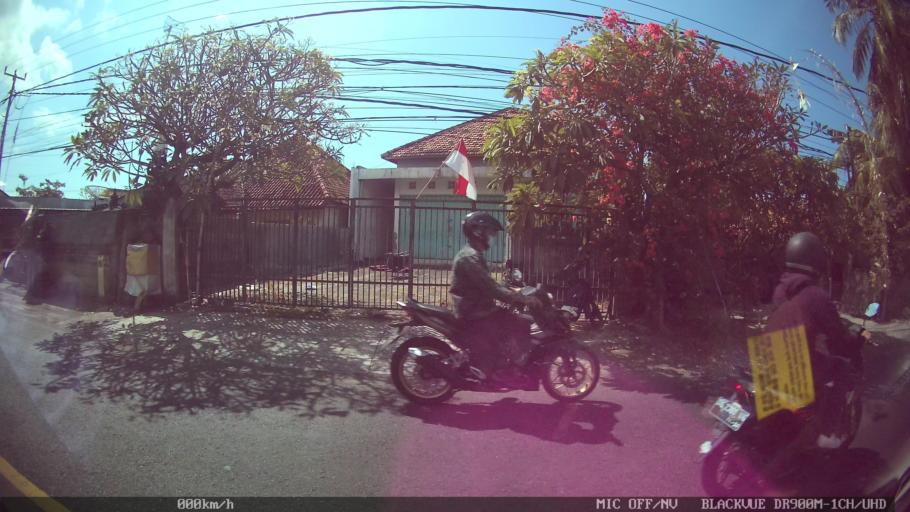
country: ID
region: Bali
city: Banjar
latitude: -8.1900
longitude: 114.9668
